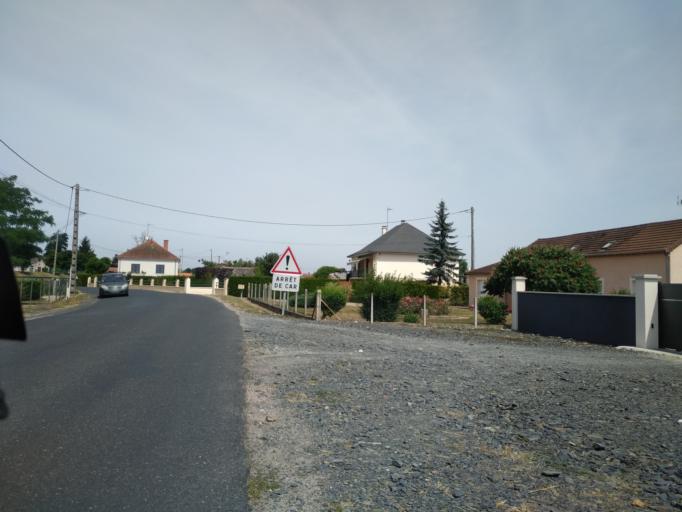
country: FR
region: Auvergne
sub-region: Departement de l'Allier
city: Molinet
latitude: 46.4513
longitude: 3.9683
